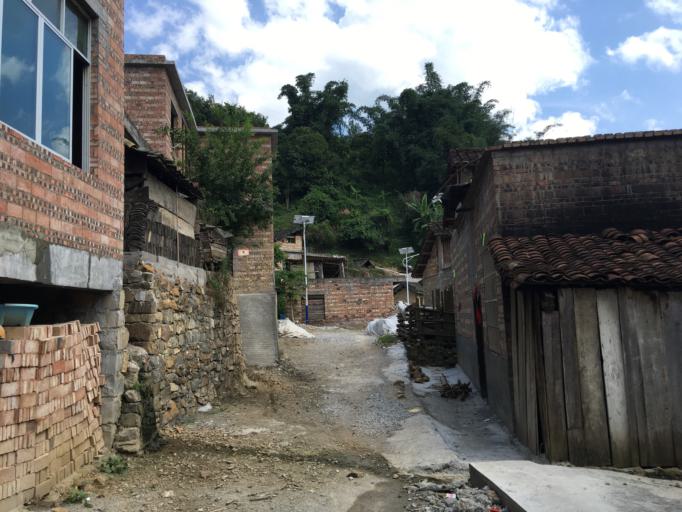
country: CN
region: Guangxi Zhuangzu Zizhiqu
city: Tongle
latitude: 24.9695
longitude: 105.9870
